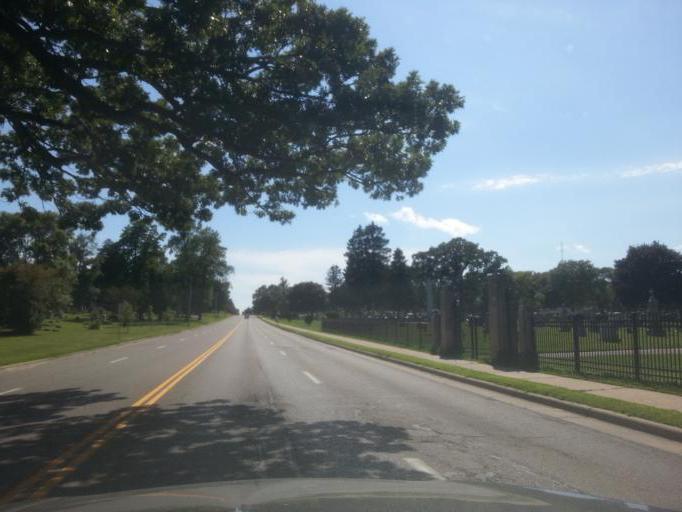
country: US
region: Wisconsin
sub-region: Dane County
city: Shorewood Hills
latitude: 43.0672
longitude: -89.4300
